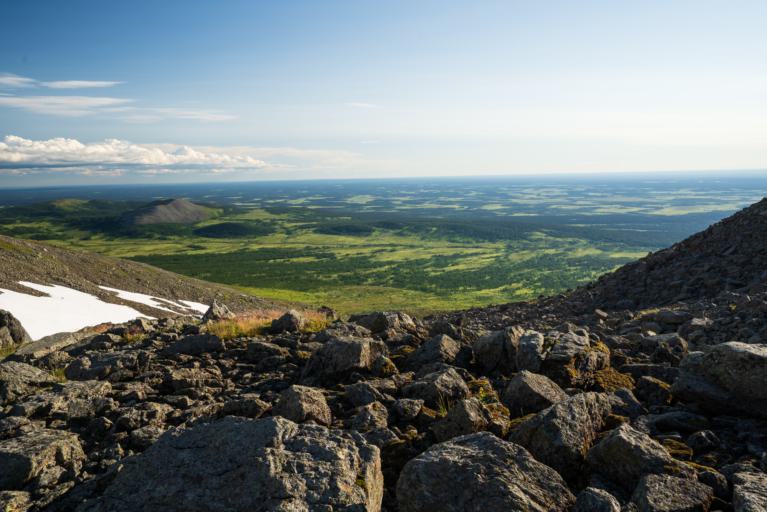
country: RU
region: Komi Republic
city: Synya
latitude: 64.7734
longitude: 58.8583
